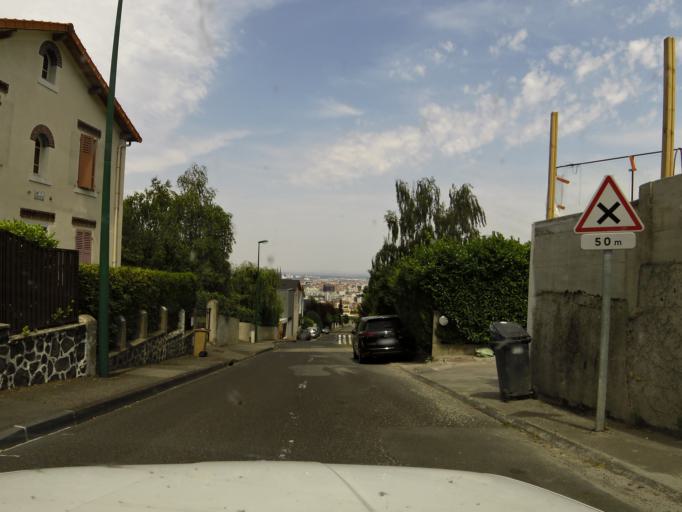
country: FR
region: Auvergne
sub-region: Departement du Puy-de-Dome
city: Chamalieres
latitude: 45.7629
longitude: 3.0672
